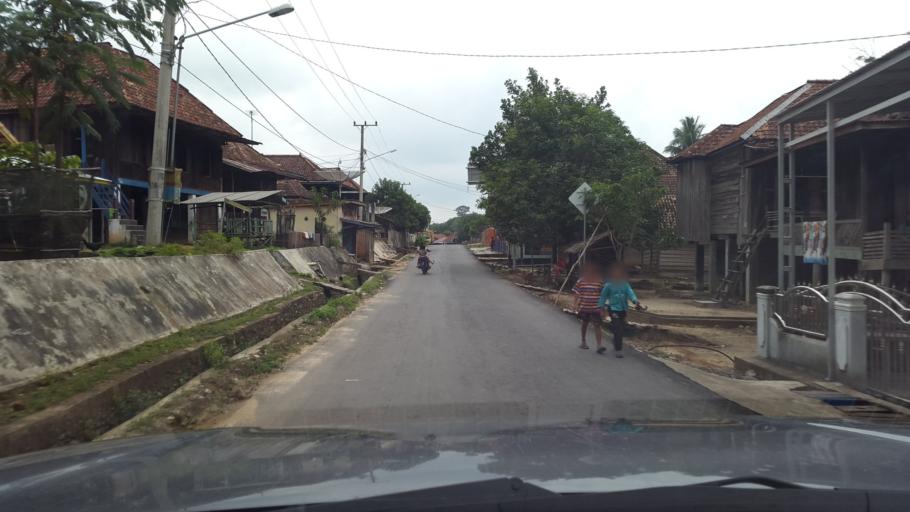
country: ID
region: South Sumatra
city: Gunungmenang
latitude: -3.1107
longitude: 103.9473
